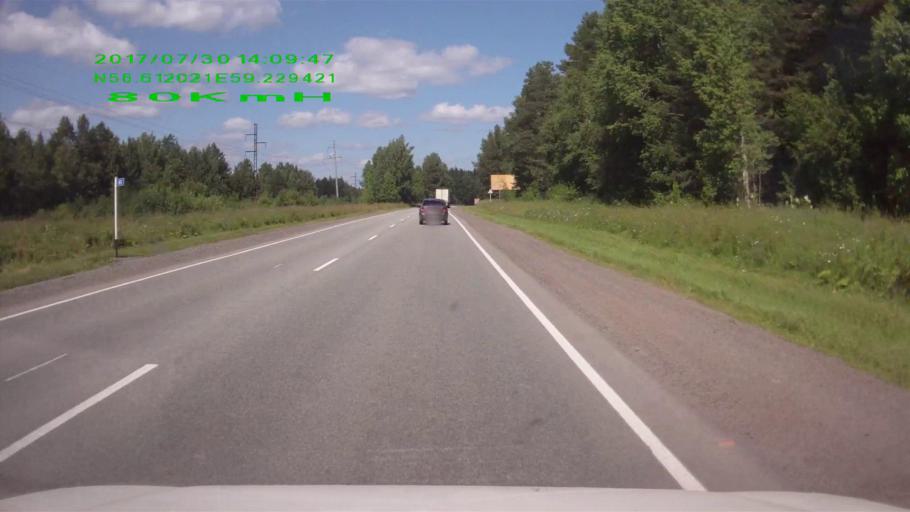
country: RU
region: Sverdlovsk
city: Nizhniye Sergi
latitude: 56.6122
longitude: 59.2295
